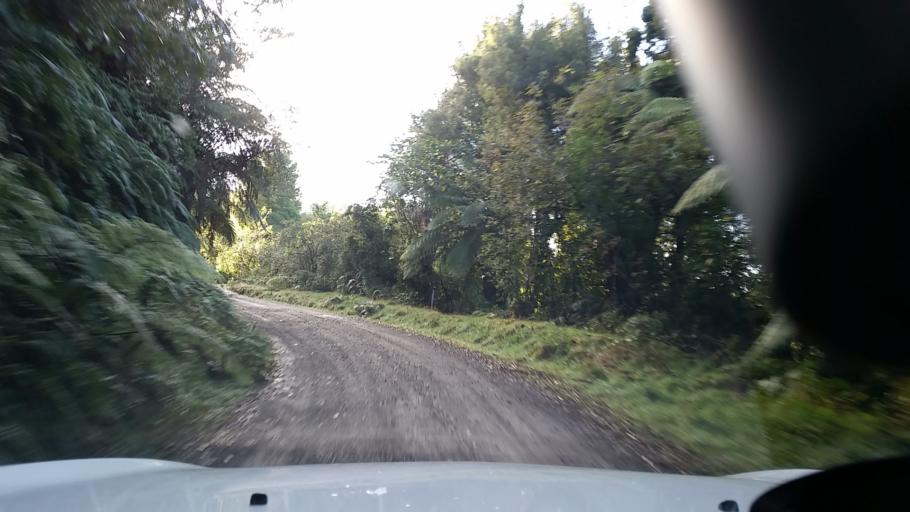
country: NZ
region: Bay of Plenty
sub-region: Kawerau District
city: Kawerau
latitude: -38.0195
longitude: 176.5875
